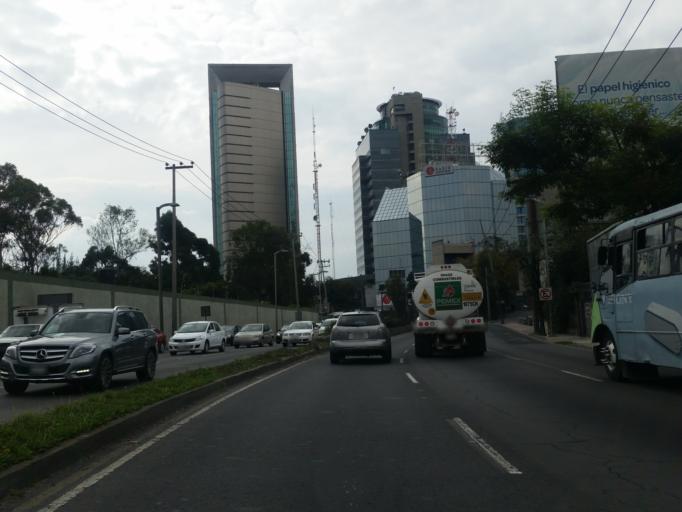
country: MX
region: Mexico City
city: Col. Bosques de las Lomas
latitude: 19.3936
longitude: -99.2362
